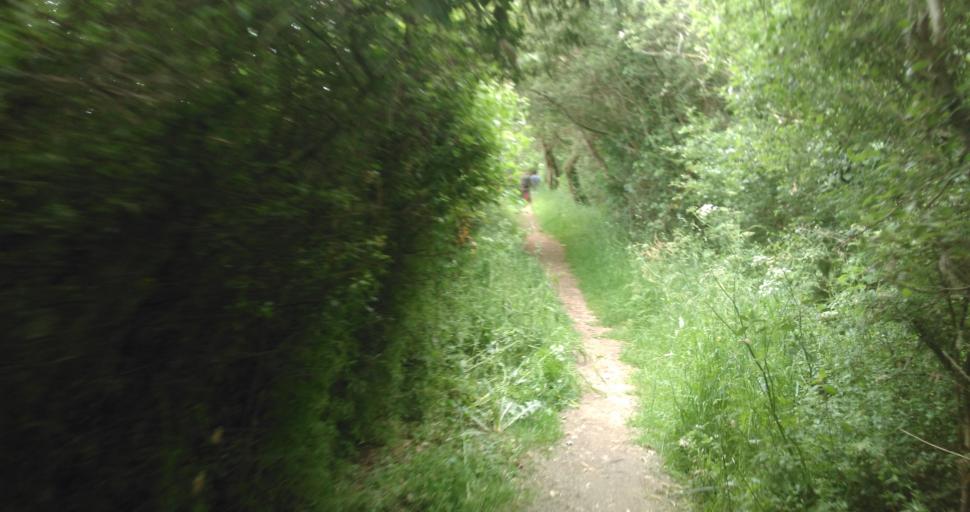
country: FR
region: Brittany
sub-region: Departement d'Ille-et-Vilaine
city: Monterfil
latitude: 48.0691
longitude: -2.0121
